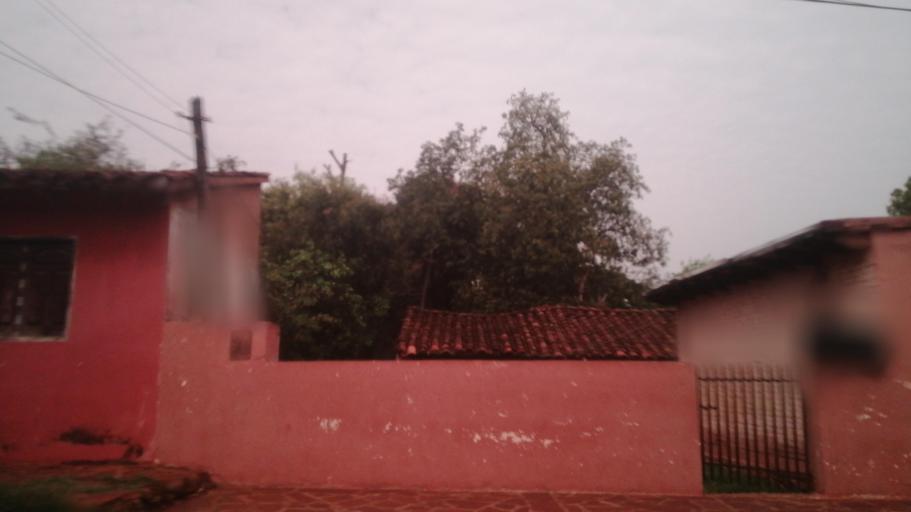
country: PY
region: Misiones
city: San Juan Bautista
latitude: -26.6732
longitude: -57.1516
